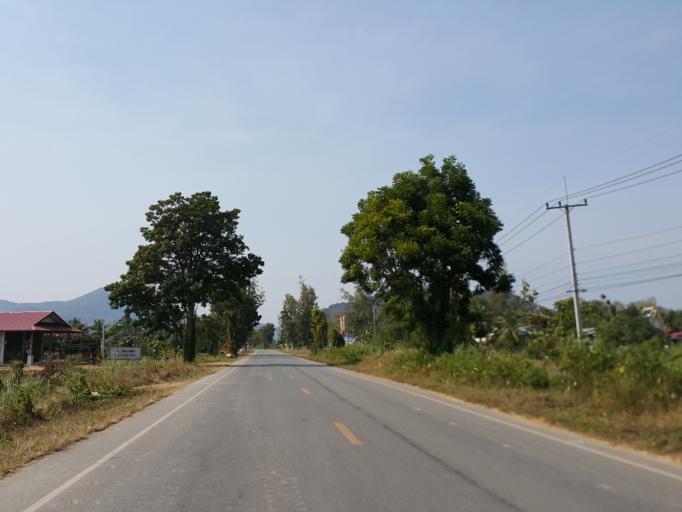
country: TH
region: Sukhothai
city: Thung Saliam
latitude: 17.3309
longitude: 99.5235
